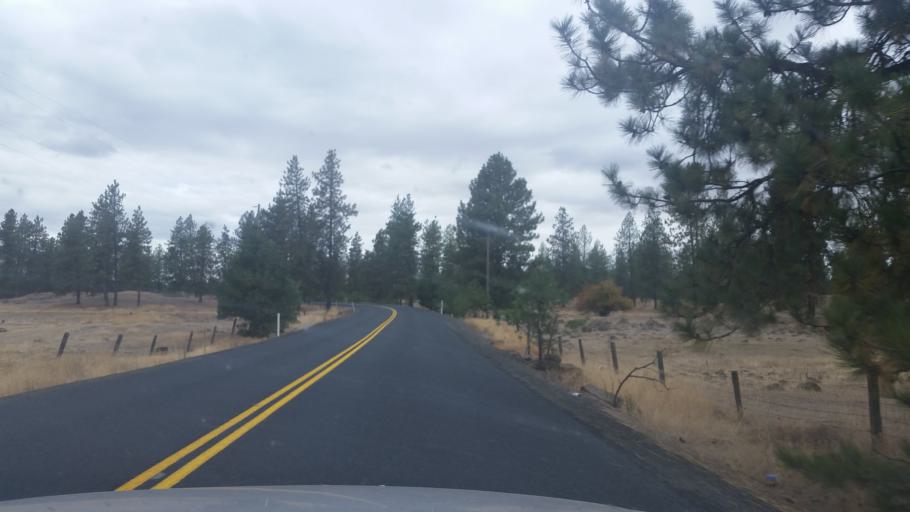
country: US
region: Washington
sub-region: Spokane County
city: Medical Lake
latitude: 47.5167
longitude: -117.7490
